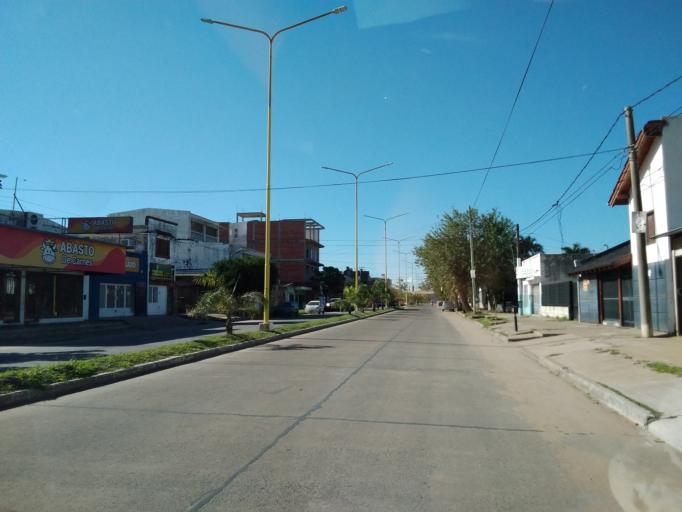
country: AR
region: Corrientes
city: Corrientes
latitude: -27.4645
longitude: -58.7885
